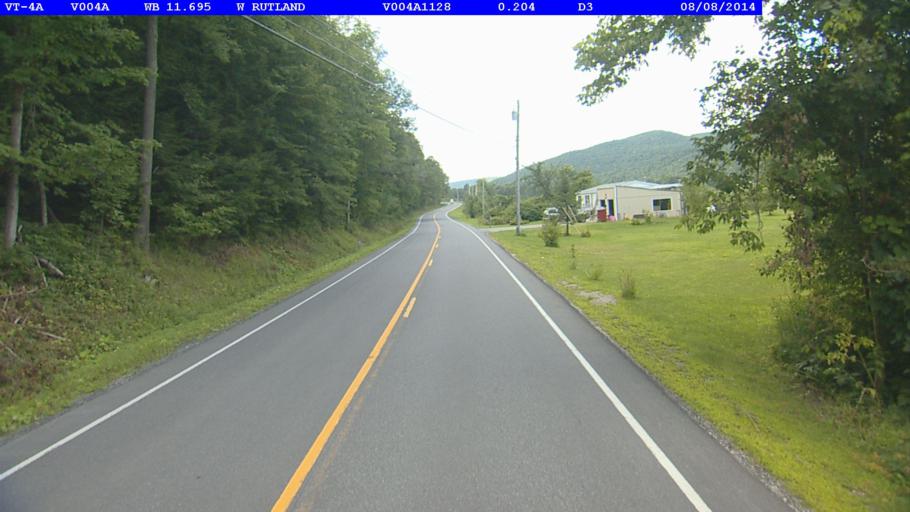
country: US
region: Vermont
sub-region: Rutland County
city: West Rutland
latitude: 43.6058
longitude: -73.0845
